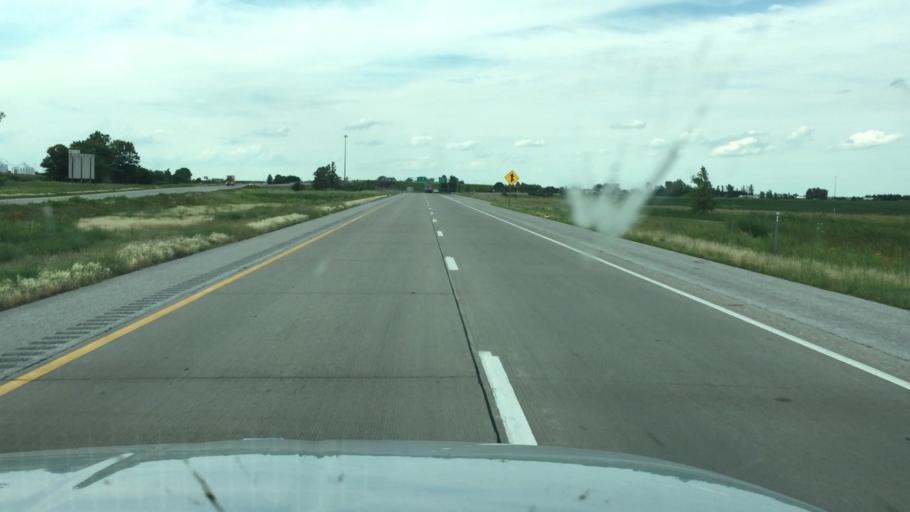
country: US
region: Iowa
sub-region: Scott County
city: Walcott
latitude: 41.5935
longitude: -90.6757
